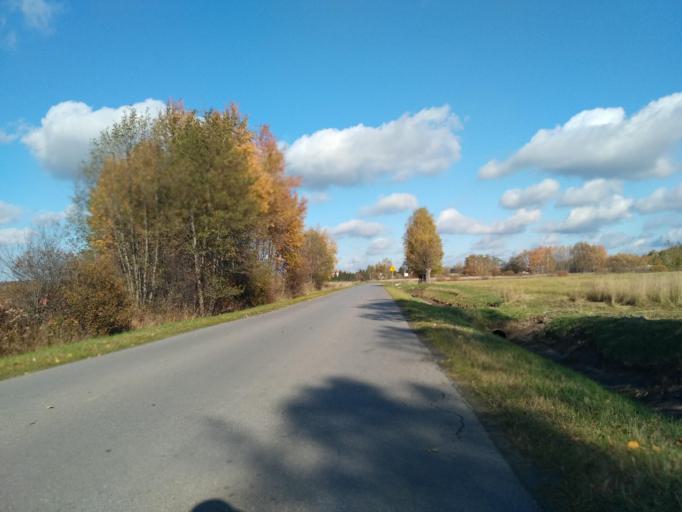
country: PL
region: Subcarpathian Voivodeship
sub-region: Powiat rzeszowski
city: Swilcza
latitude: 50.1275
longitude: 21.9023
